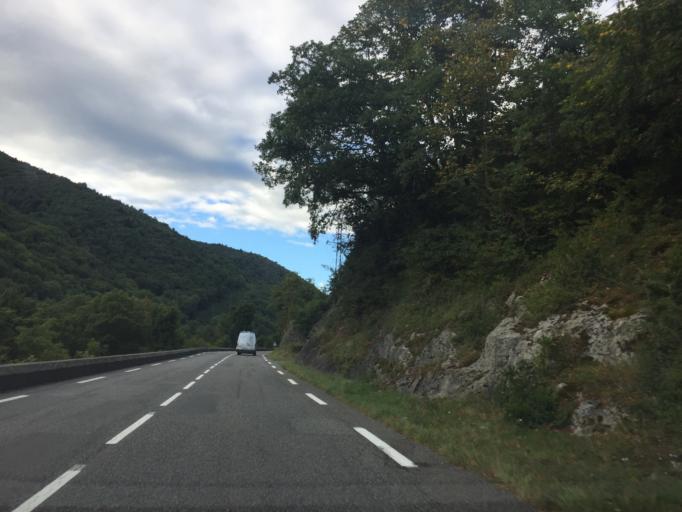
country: FR
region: Midi-Pyrenees
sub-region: Departement des Hautes-Pyrenees
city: Saint-Lary-Soulan
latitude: 42.9297
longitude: 0.3675
